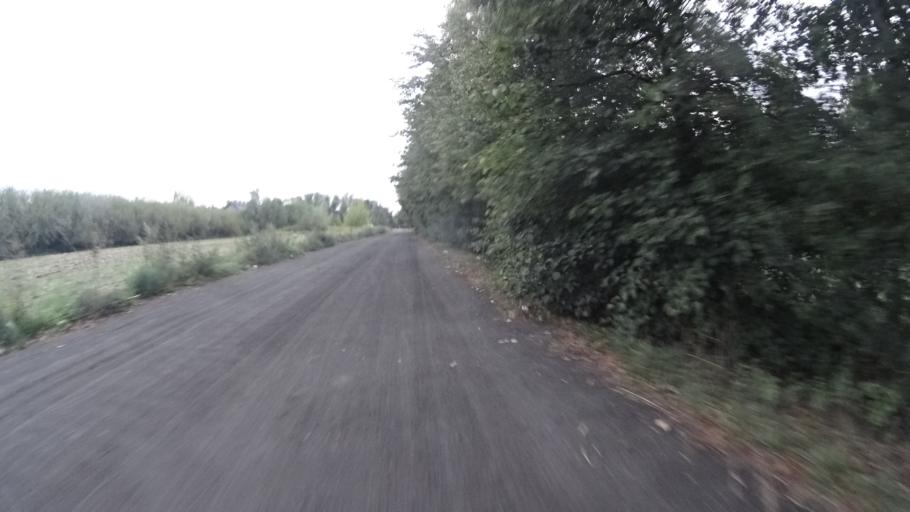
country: PL
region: Masovian Voivodeship
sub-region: Powiat warszawski zachodni
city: Ozarow Mazowiecki
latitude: 52.2332
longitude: 20.7654
